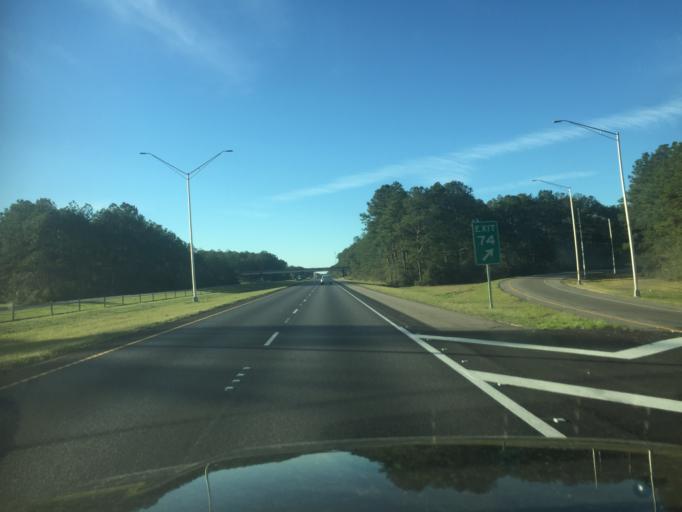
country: US
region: Louisiana
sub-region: Saint Tammany Parish
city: Lacombe
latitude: 30.3506
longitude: -89.9170
